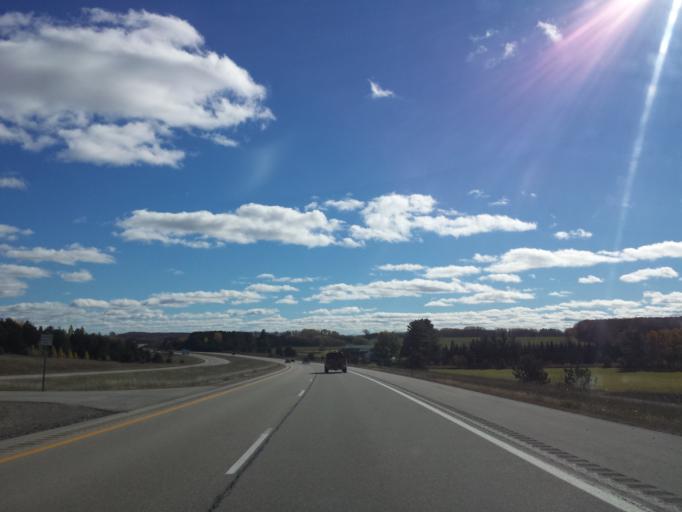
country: US
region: Michigan
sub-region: Cheboygan County
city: Cheboygan
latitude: 45.6240
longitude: -84.6341
